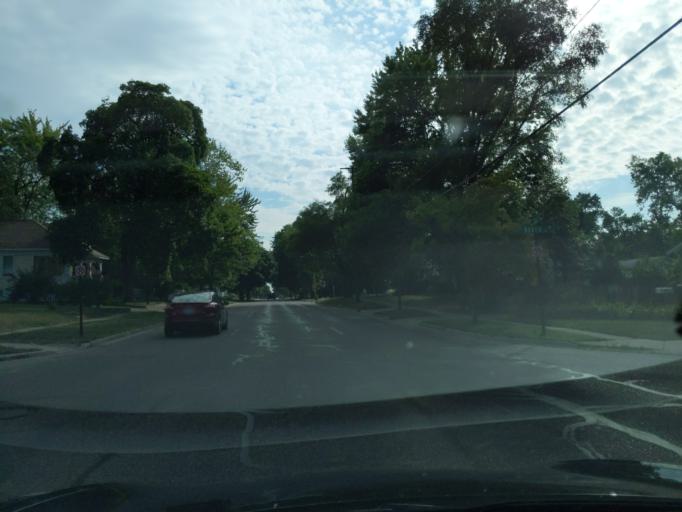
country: US
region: Michigan
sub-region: Midland County
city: Midland
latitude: 43.6203
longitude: -84.2355
